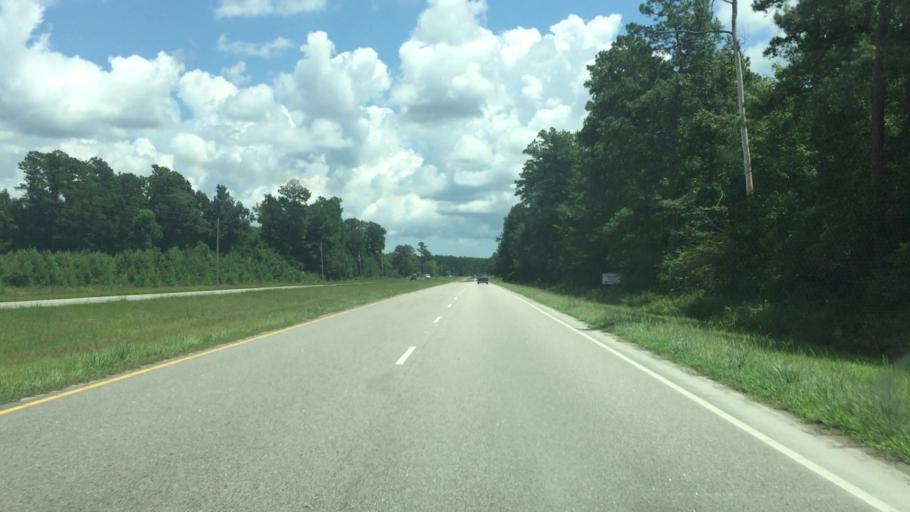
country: US
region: South Carolina
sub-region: Horry County
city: Loris
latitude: 34.0107
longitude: -78.7736
